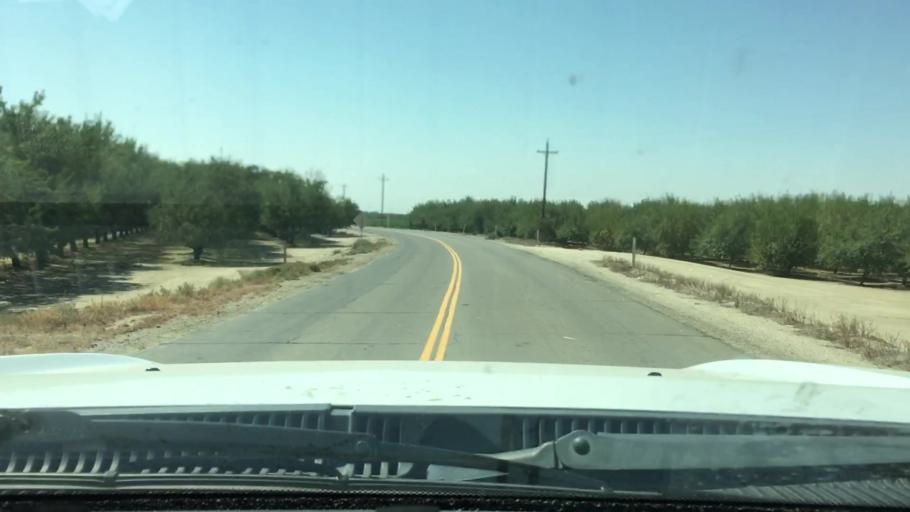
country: US
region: California
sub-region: Kern County
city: Shafter
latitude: 35.5490
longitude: -119.2773
